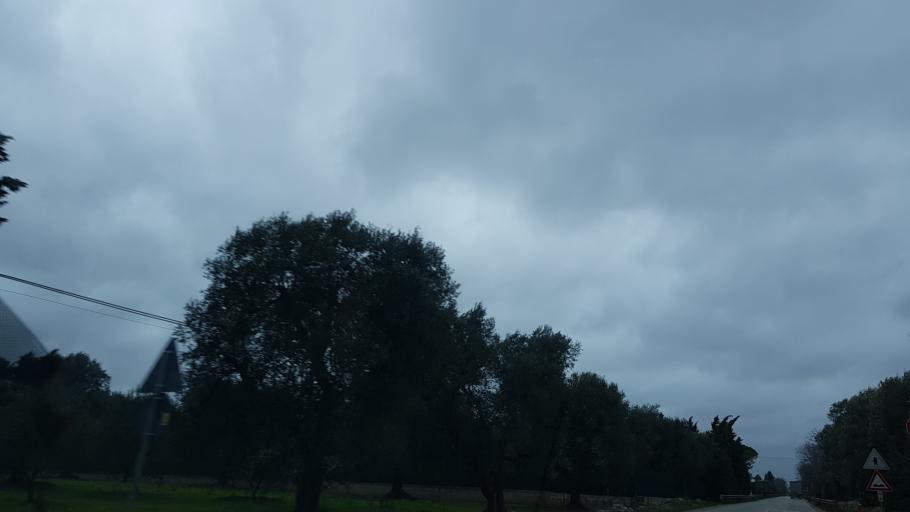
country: IT
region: Apulia
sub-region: Provincia di Brindisi
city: San Vito dei Normanni
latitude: 40.6562
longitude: 17.7427
